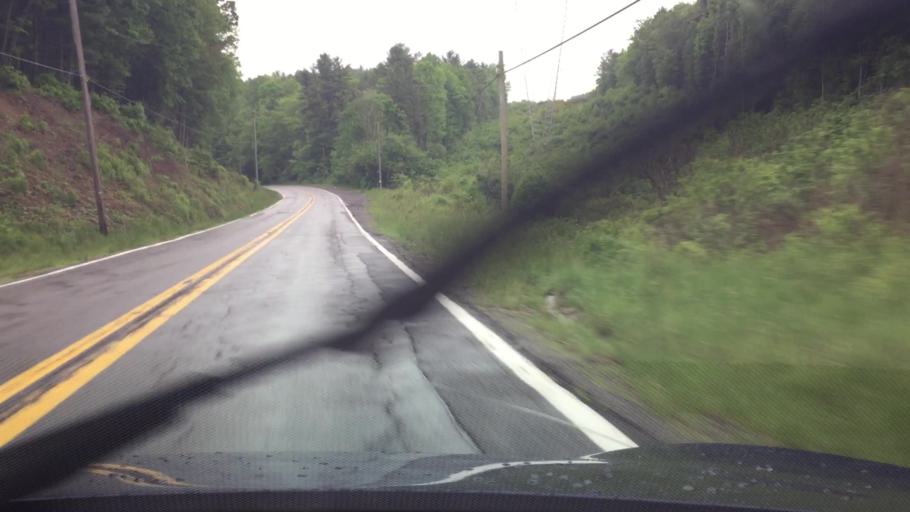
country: US
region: West Virginia
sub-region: Raleigh County
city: Shady Spring
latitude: 37.6881
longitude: -81.0595
